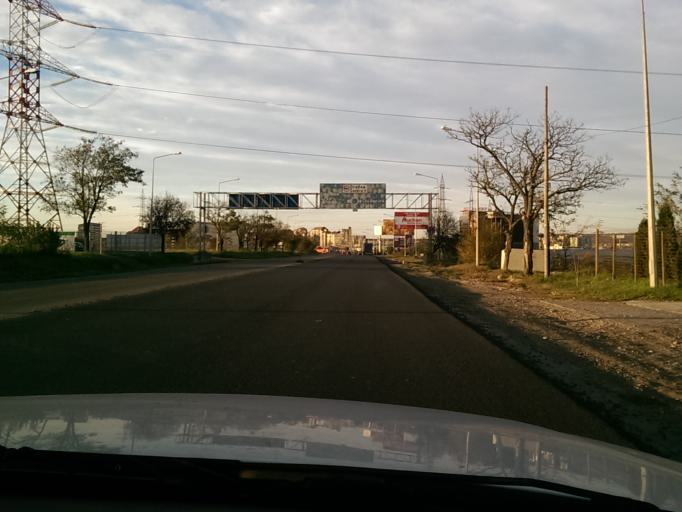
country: RO
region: Bihor
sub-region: Comuna Sanmartin
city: Sanmartin
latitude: 47.0214
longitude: 21.9620
